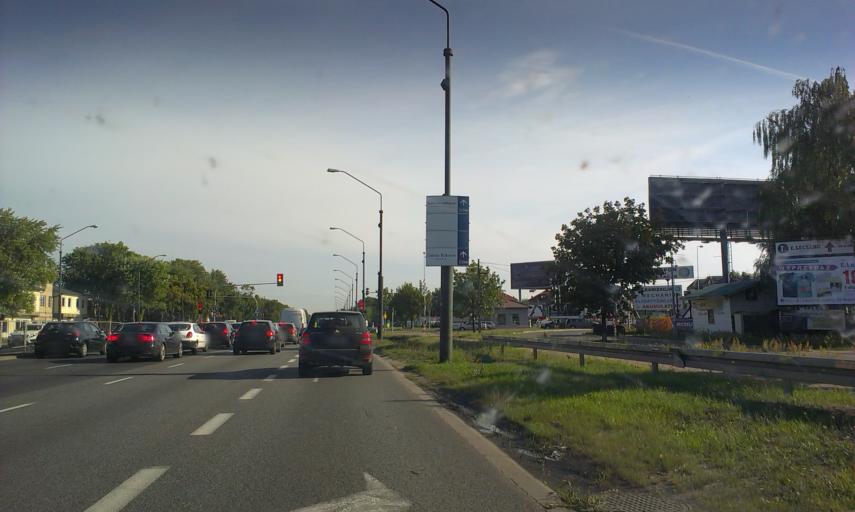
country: PL
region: Masovian Voivodeship
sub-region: Warszawa
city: Ursynow
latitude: 52.1427
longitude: 21.0180
